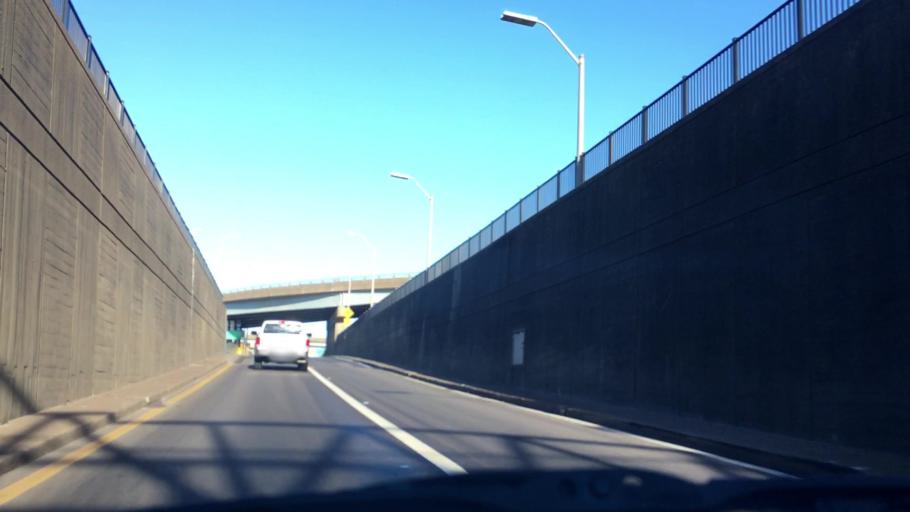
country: US
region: Virginia
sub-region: City of Norfolk
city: Norfolk
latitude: 36.8624
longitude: -76.3079
